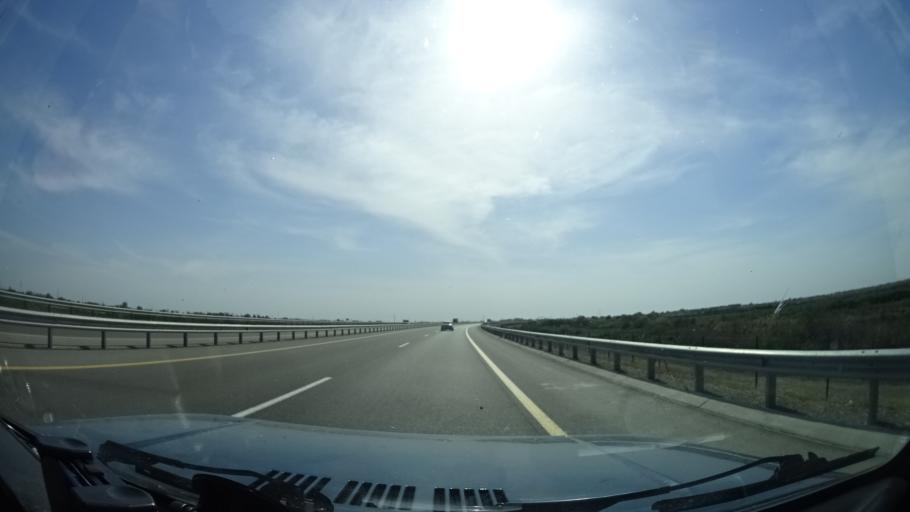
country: AZ
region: Salyan
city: Salyan
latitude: 39.6359
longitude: 48.9992
